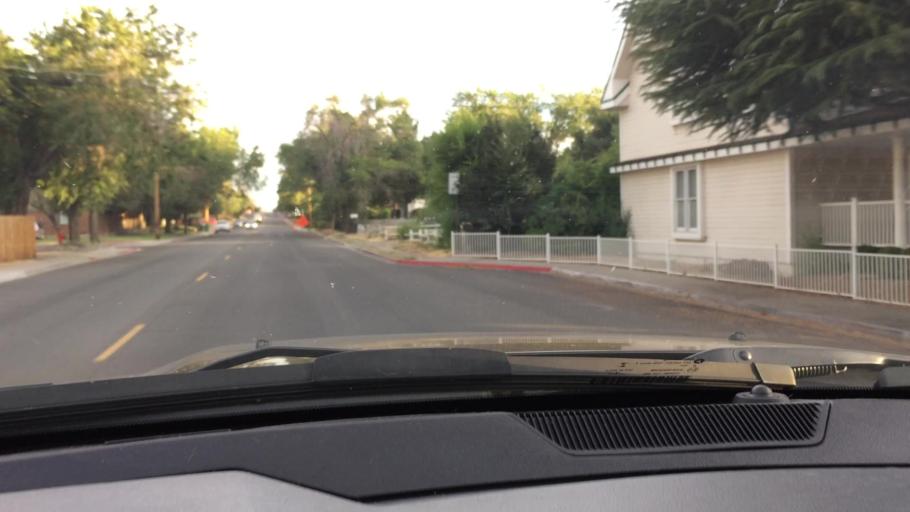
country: US
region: Nevada
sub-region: Washoe County
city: Reno
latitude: 39.5095
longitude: -119.8127
